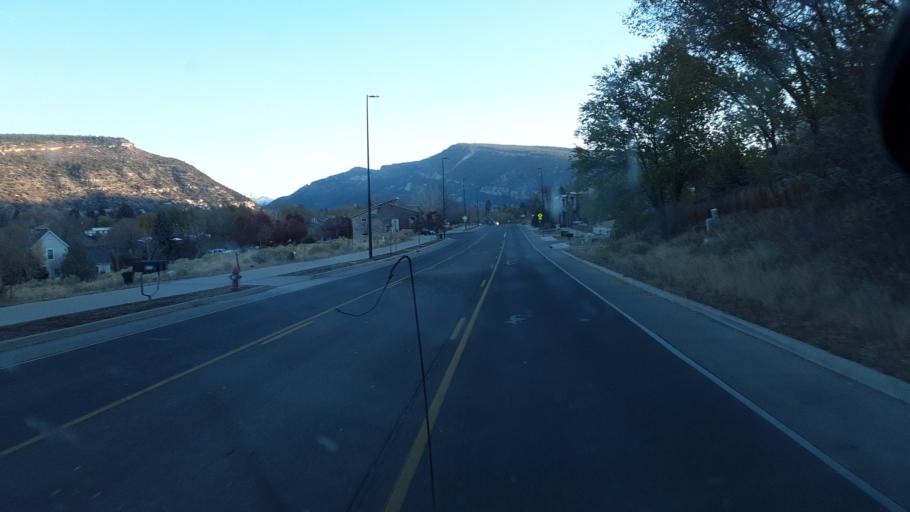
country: US
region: Colorado
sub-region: La Plata County
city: Durango
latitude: 37.2886
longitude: -107.8650
